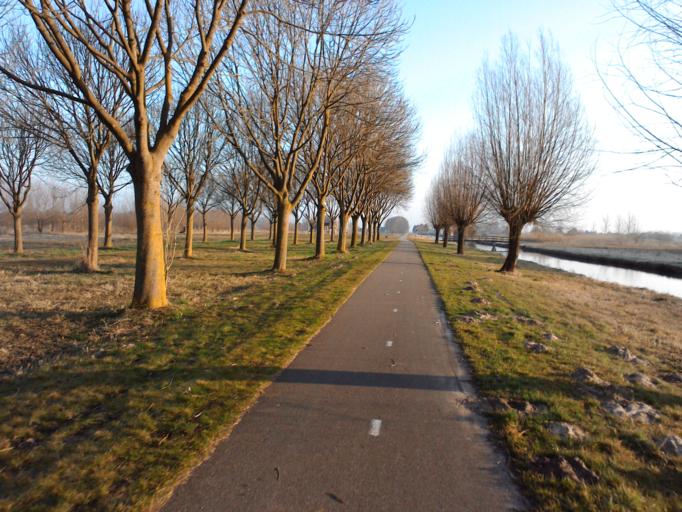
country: NL
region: Utrecht
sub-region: Gemeente Utrecht
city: Utrecht
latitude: 52.1206
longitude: 5.1299
